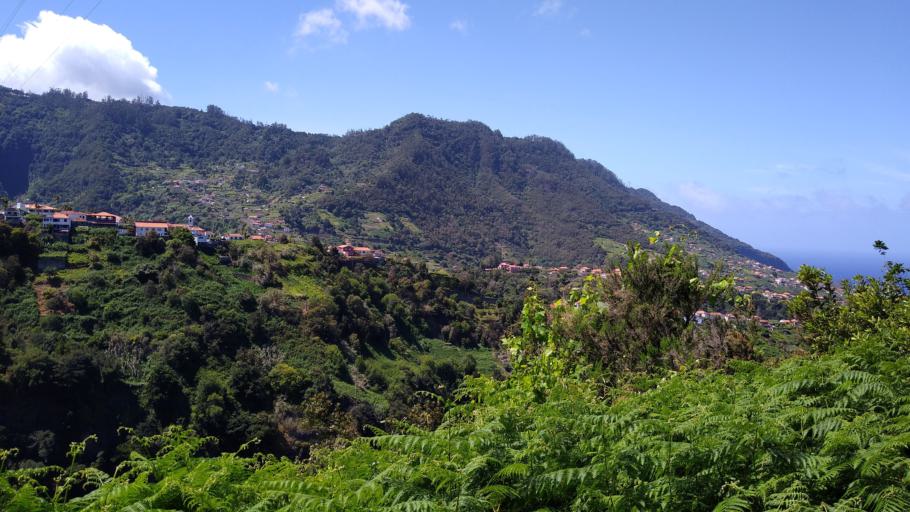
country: PT
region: Madeira
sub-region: Santana
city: Santana
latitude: 32.7680
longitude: -16.8523
